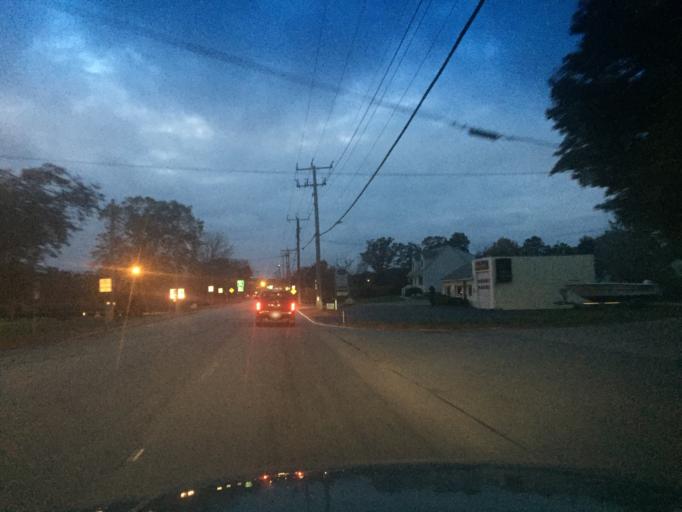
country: US
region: Massachusetts
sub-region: Plymouth County
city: Onset
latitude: 41.7619
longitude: -70.6739
